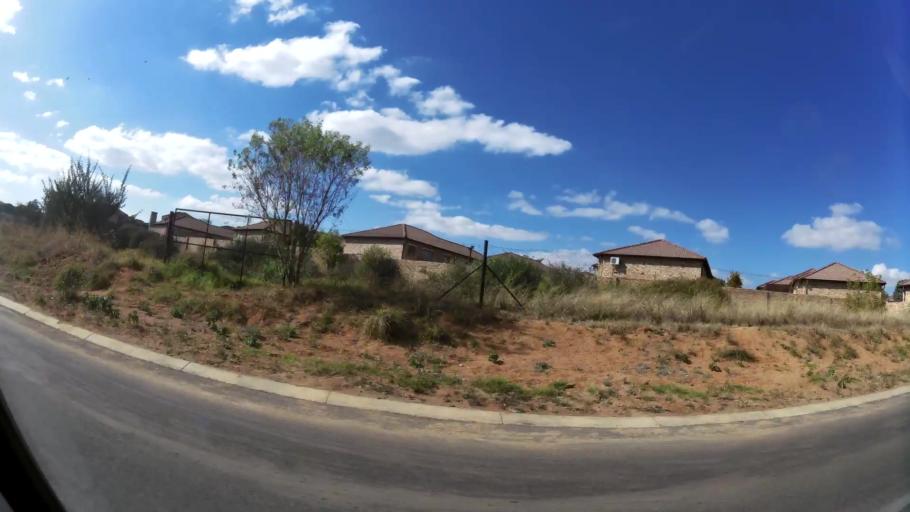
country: ZA
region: Gauteng
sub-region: City of Johannesburg Metropolitan Municipality
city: Midrand
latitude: -25.9990
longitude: 28.0936
